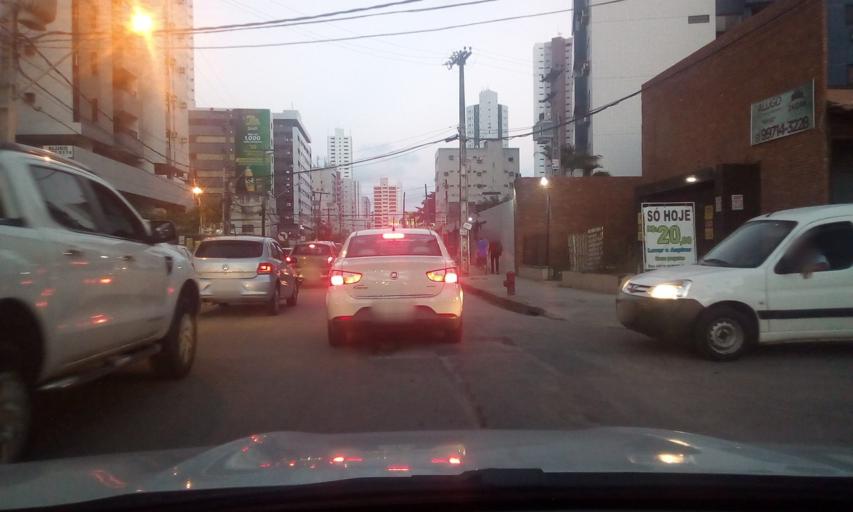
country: BR
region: Pernambuco
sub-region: Recife
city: Recife
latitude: -8.1243
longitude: -34.9078
